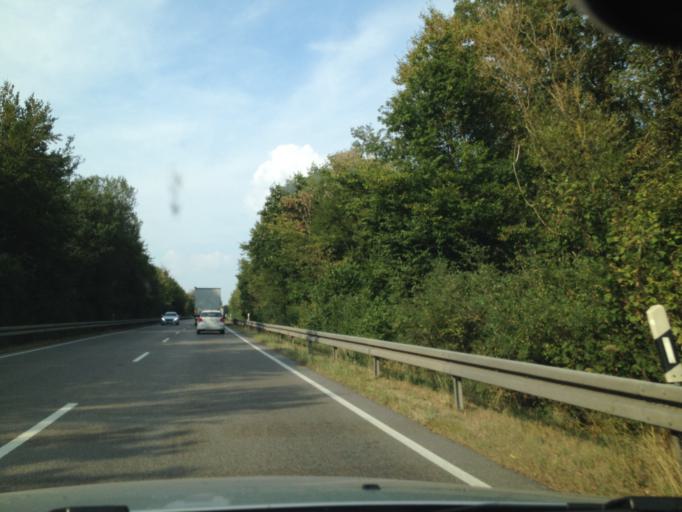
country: DE
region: Bavaria
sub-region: Swabia
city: Monheim
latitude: 48.8388
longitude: 10.8314
